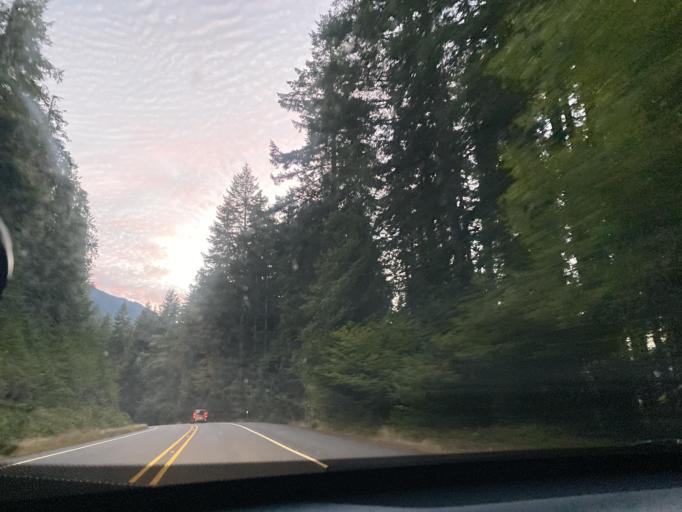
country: CA
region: British Columbia
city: Sooke
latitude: 48.0508
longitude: -123.7997
